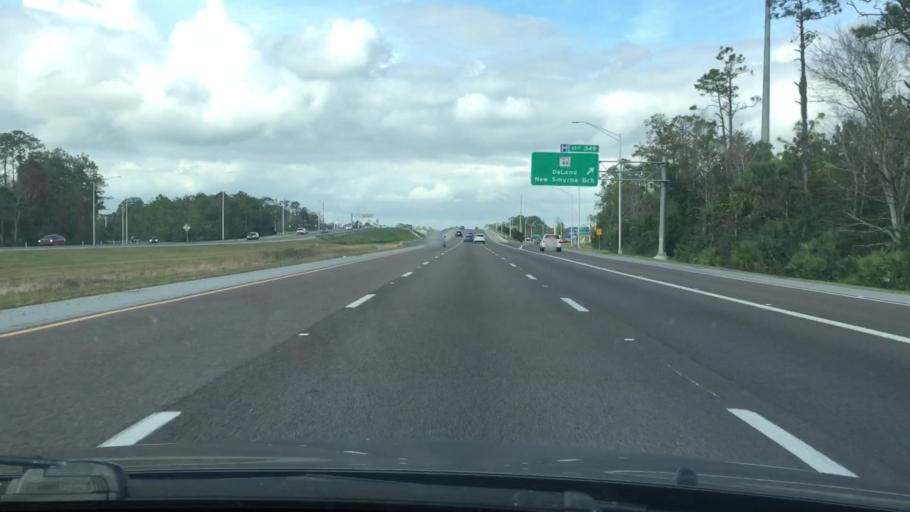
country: US
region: Florida
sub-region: Volusia County
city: Glencoe
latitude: 29.0089
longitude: -80.9851
